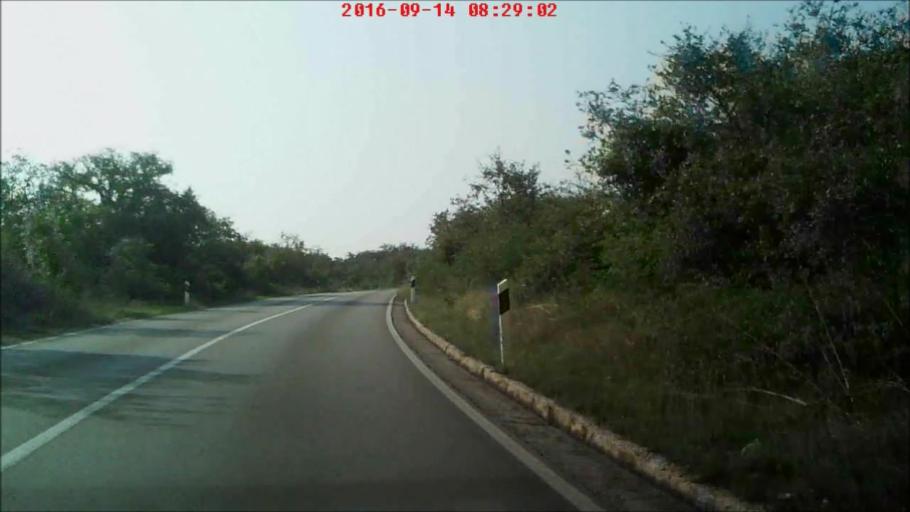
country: HR
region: Zadarska
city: Zadar
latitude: 44.1823
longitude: 15.2811
